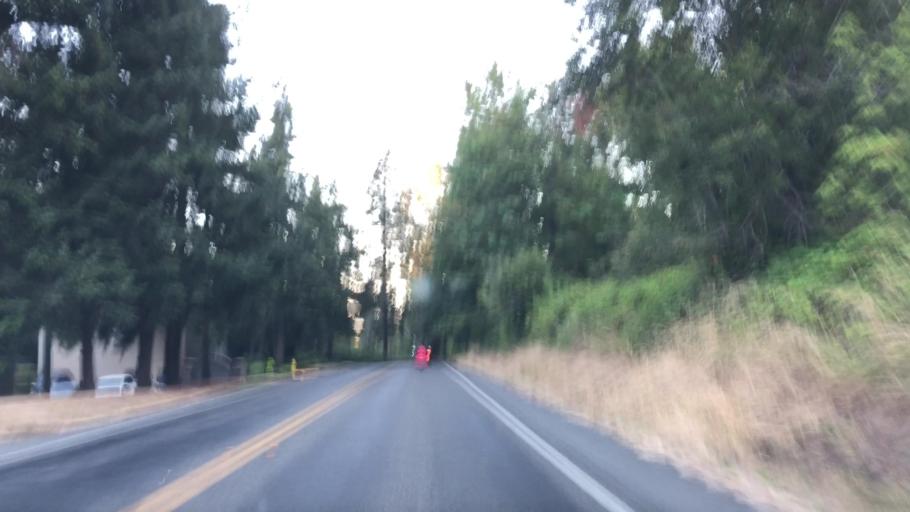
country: US
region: Washington
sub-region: King County
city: Lea Hill
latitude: 47.3145
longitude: -122.2003
